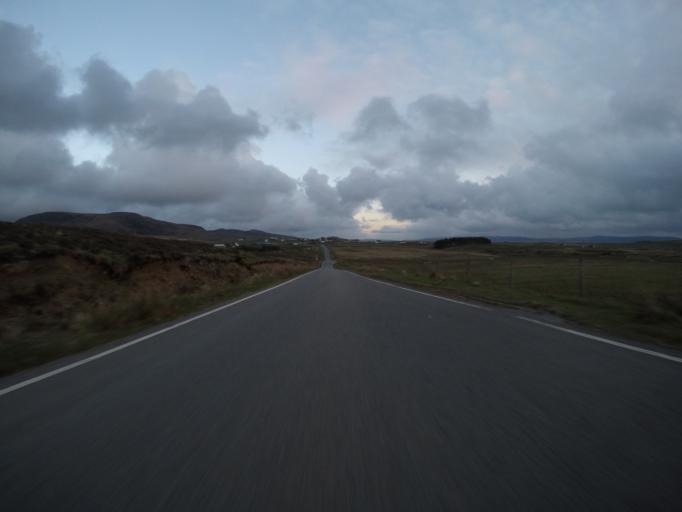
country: GB
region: Scotland
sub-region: Highland
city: Portree
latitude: 57.6522
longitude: -6.3801
